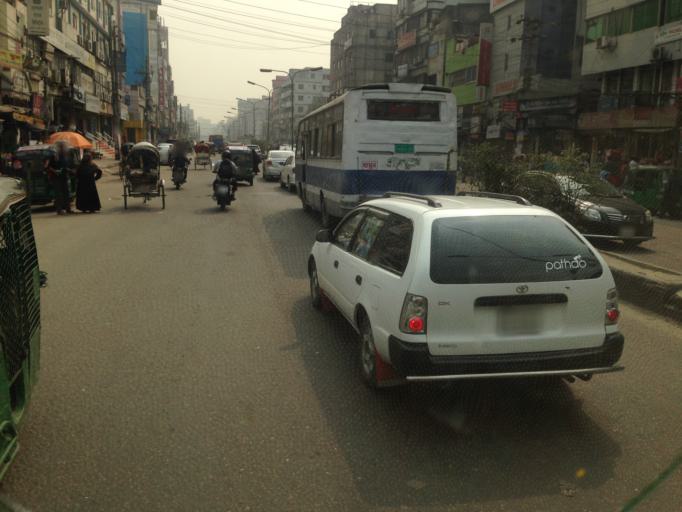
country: BD
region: Dhaka
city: Tungi
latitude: 23.8166
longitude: 90.4211
